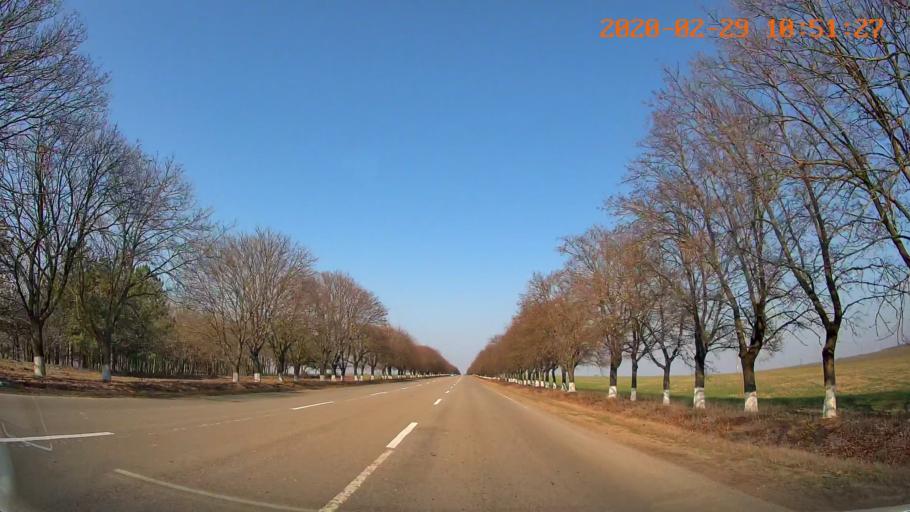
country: MD
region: Telenesti
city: Grigoriopol
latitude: 47.0933
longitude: 29.3641
